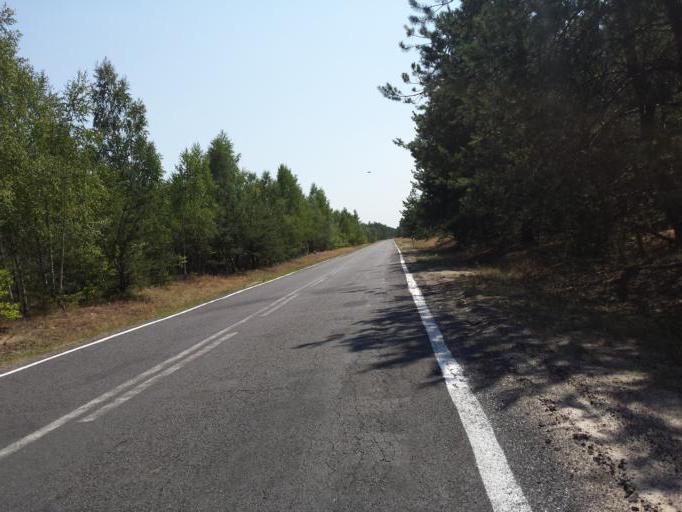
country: PL
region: Lublin Voivodeship
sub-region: Powiat bialski
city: Koden
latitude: 51.8729
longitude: 23.5953
